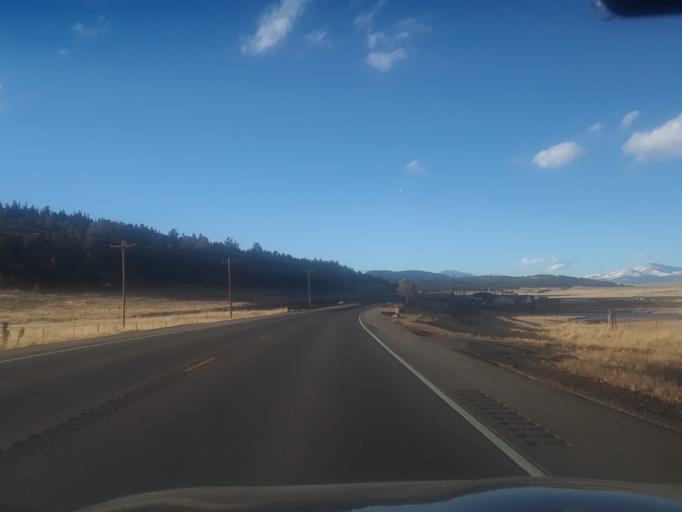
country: US
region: Colorado
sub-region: Park County
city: Fairplay
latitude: 39.0053
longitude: -105.9681
